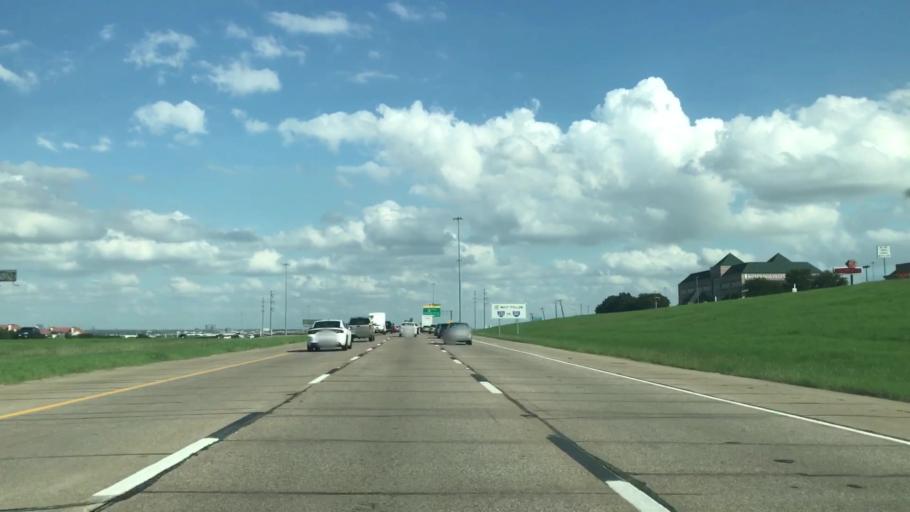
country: US
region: Texas
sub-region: Dallas County
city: Farmers Branch
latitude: 32.9143
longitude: -96.9548
